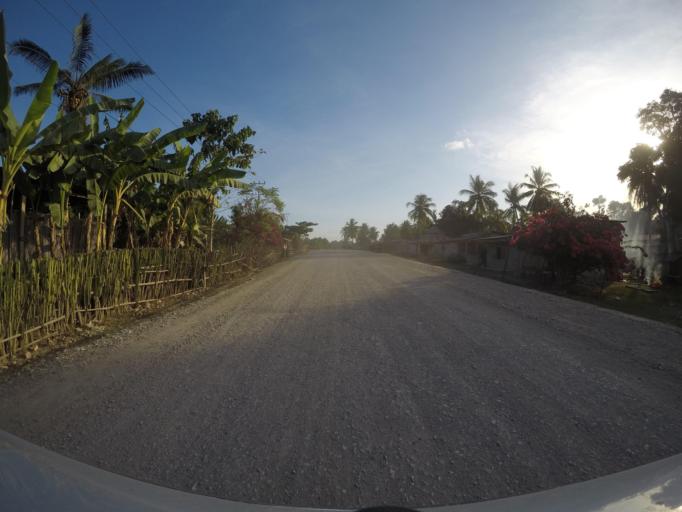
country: TL
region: Viqueque
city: Viqueque
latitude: -8.8267
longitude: 126.5279
